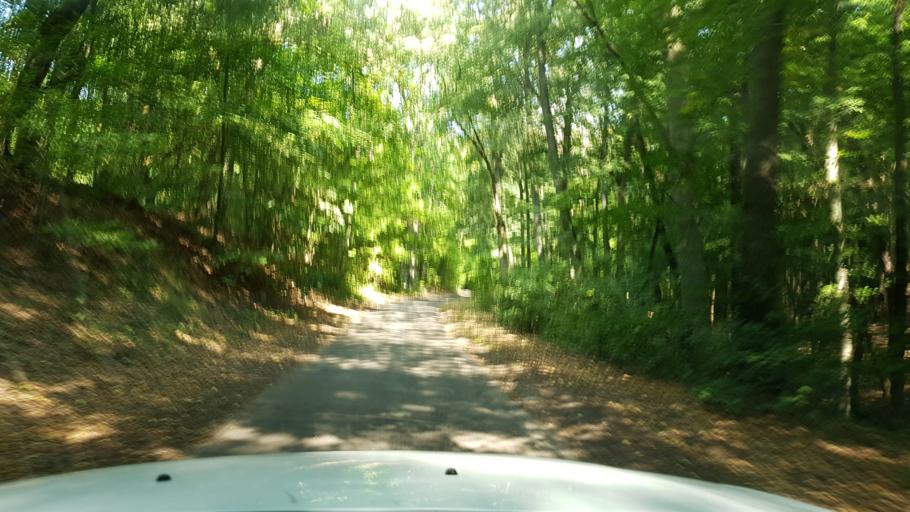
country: DE
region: Brandenburg
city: Neulewin
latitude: 52.8022
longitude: 14.3121
